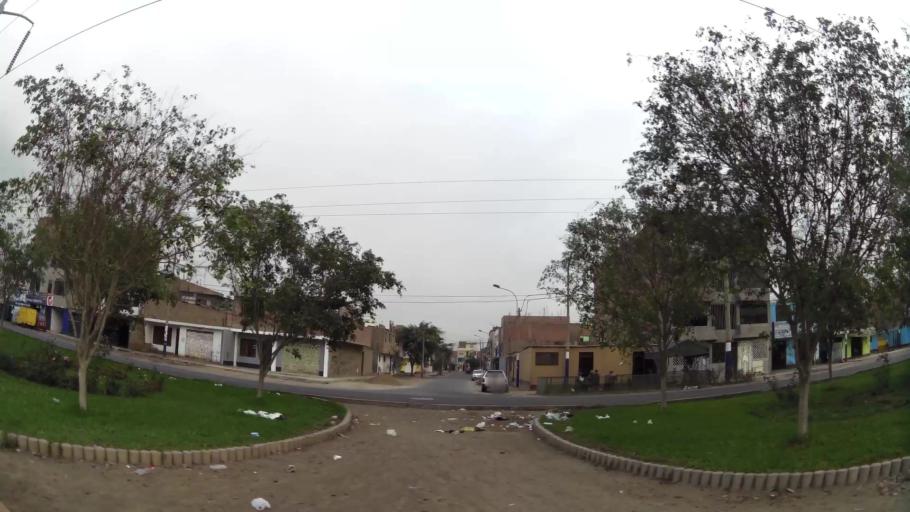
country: PE
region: Lima
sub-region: Lima
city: Independencia
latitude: -11.9962
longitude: -77.0043
